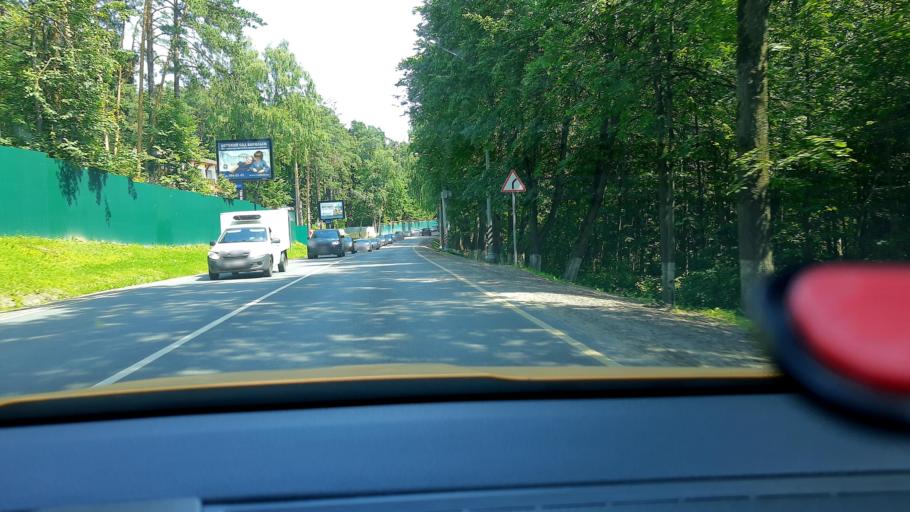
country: RU
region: Moskovskaya
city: Arkhangel'skoye
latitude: 55.7803
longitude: 37.2577
